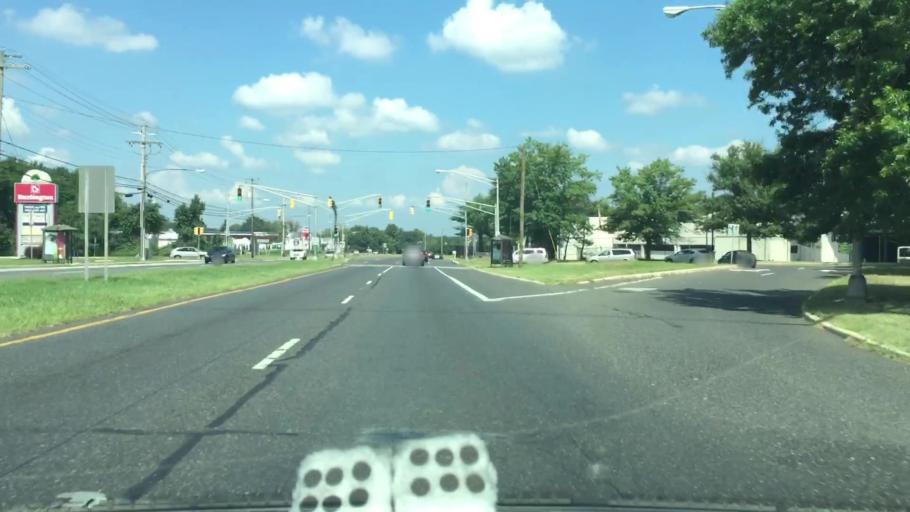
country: US
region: New Jersey
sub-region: Gloucester County
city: Turnersville
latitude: 39.7642
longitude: -75.0482
